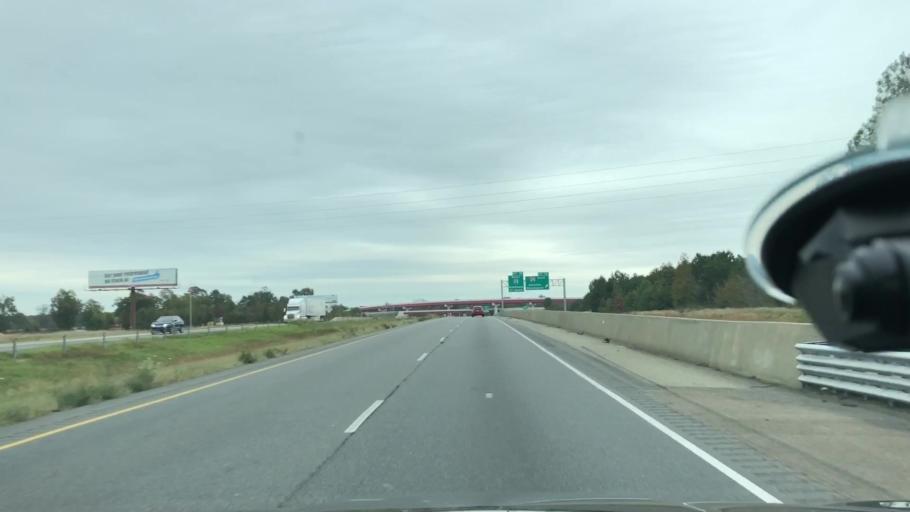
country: US
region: Arkansas
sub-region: Miller County
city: Texarkana
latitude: 33.4781
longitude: -93.9946
